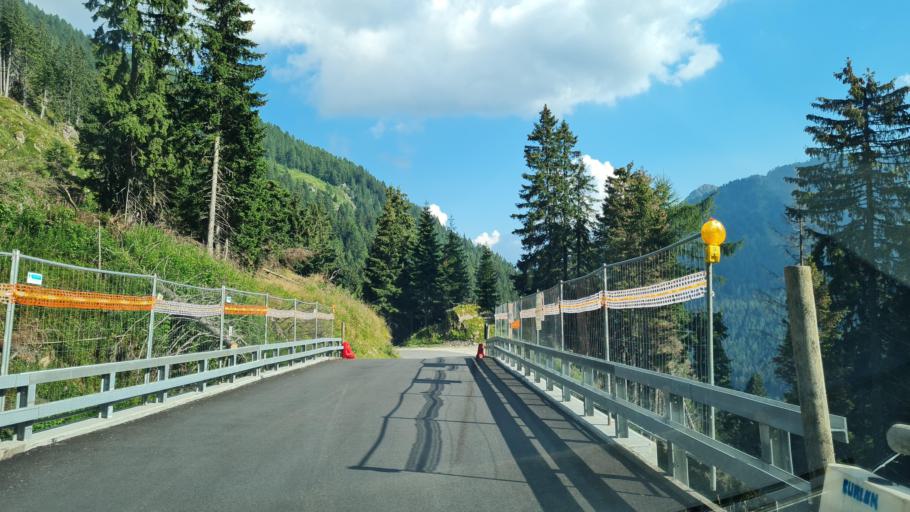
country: IT
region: Trentino-Alto Adige
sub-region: Provincia di Trento
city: Palu del Fersina
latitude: 46.1641
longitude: 11.4342
